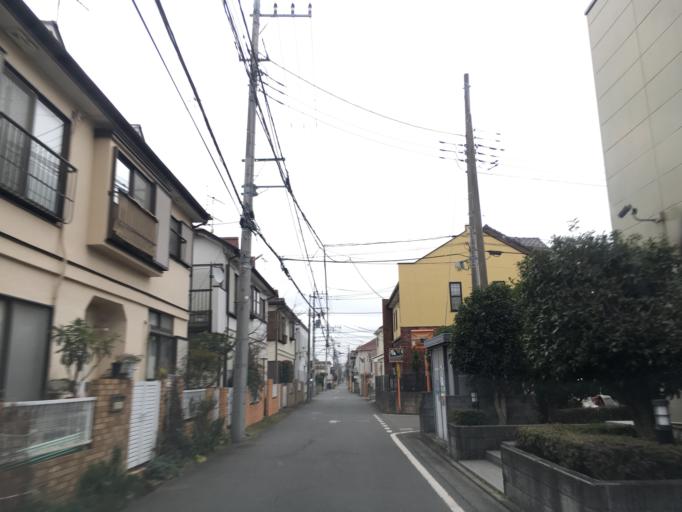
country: JP
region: Tokyo
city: Kokubunji
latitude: 35.7226
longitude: 139.4473
